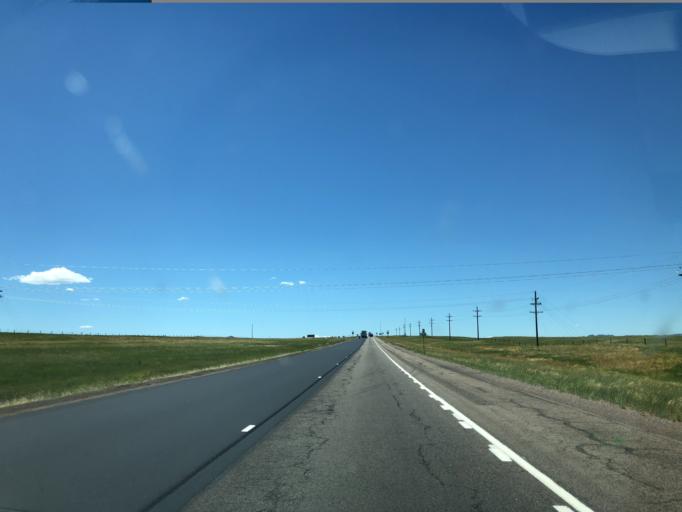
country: US
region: Wyoming
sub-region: Laramie County
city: Cheyenne
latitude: 41.1003
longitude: -105.0697
